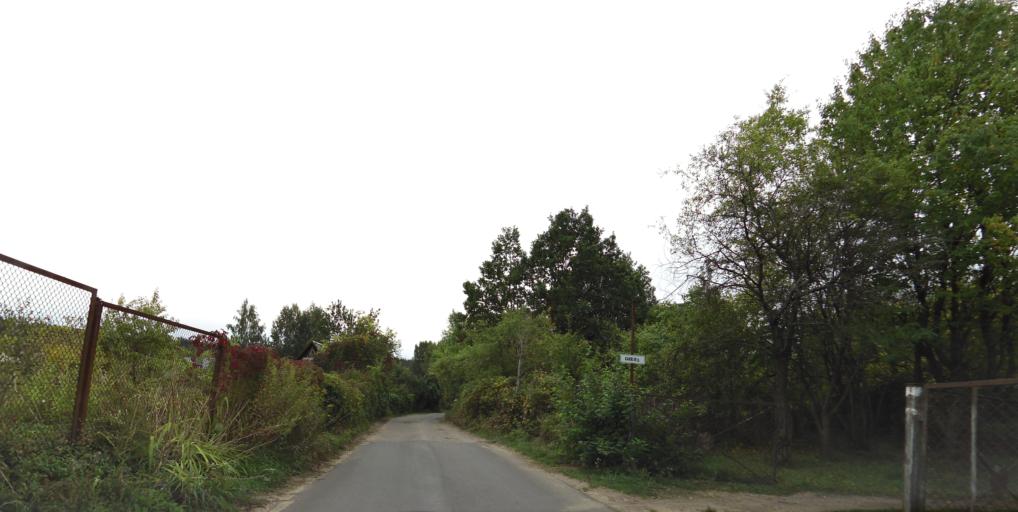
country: LT
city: Grigiskes
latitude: 54.7566
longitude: 25.0284
